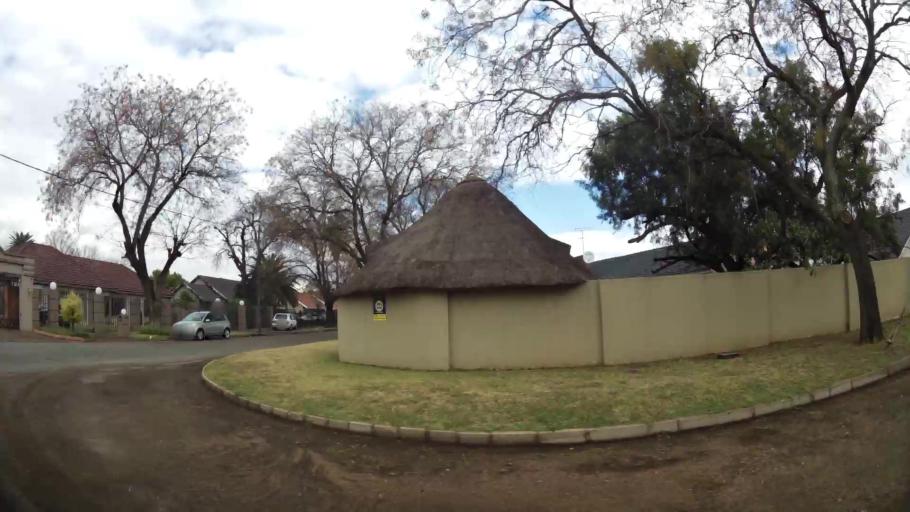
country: ZA
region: Gauteng
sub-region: Sedibeng District Municipality
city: Vereeniging
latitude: -26.6440
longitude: 27.9752
